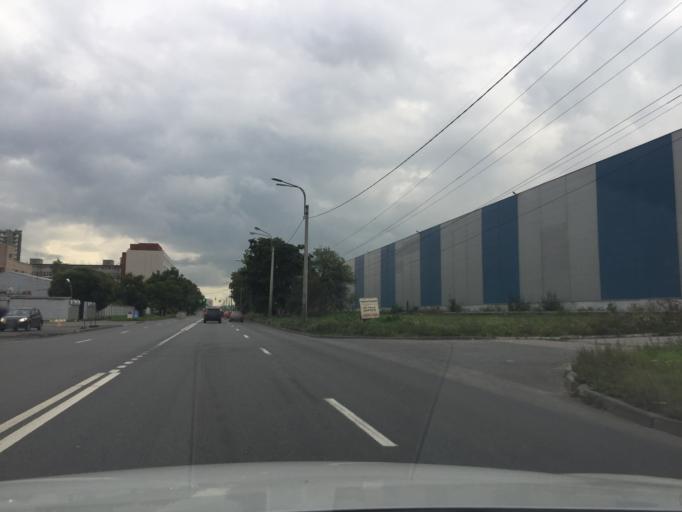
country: RU
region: St.-Petersburg
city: Dachnoye
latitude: 59.8440
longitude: 30.2952
